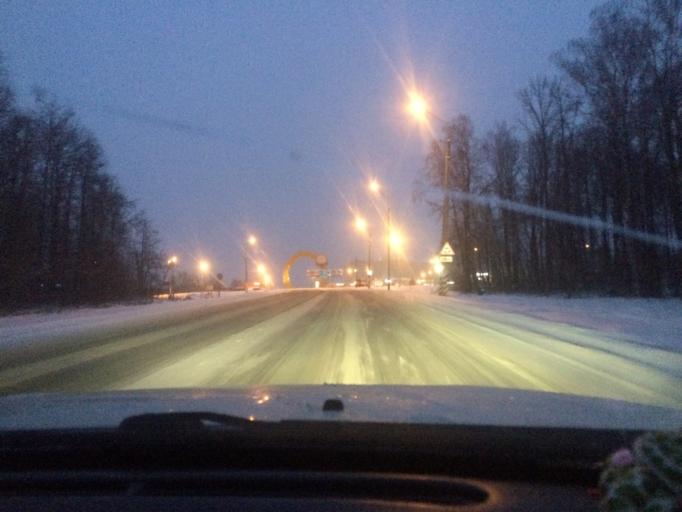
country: RU
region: Tula
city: Kosaya Gora
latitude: 54.1655
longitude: 37.4638
